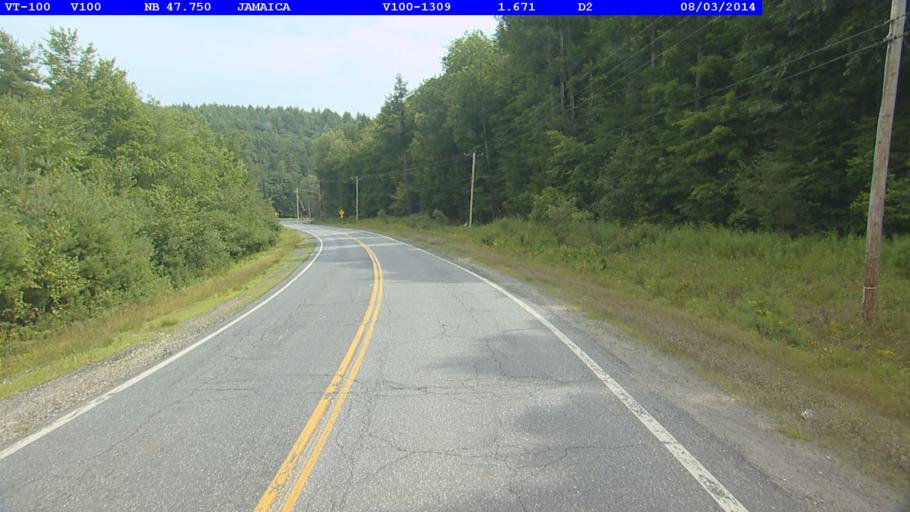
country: US
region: Vermont
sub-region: Windham County
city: Dover
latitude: 43.0618
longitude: -72.7627
